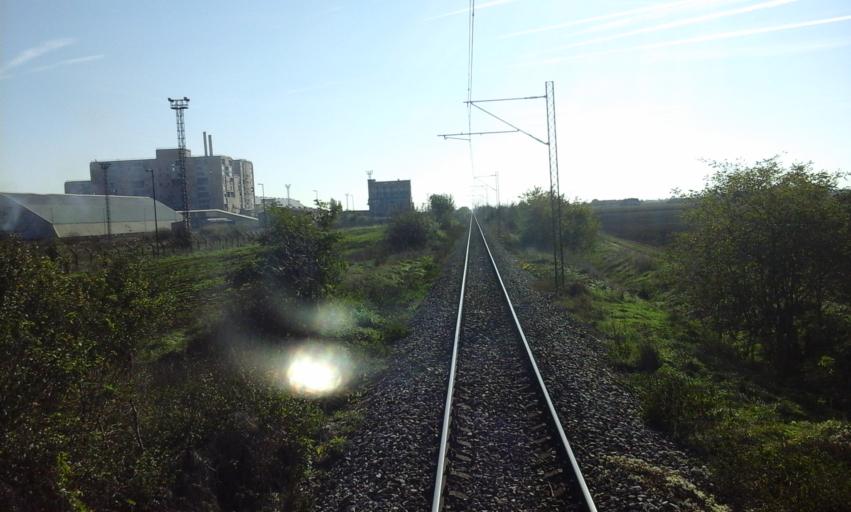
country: RS
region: Autonomna Pokrajina Vojvodina
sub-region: Severnobacki Okrug
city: Subotica
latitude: 46.0094
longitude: 19.6790
